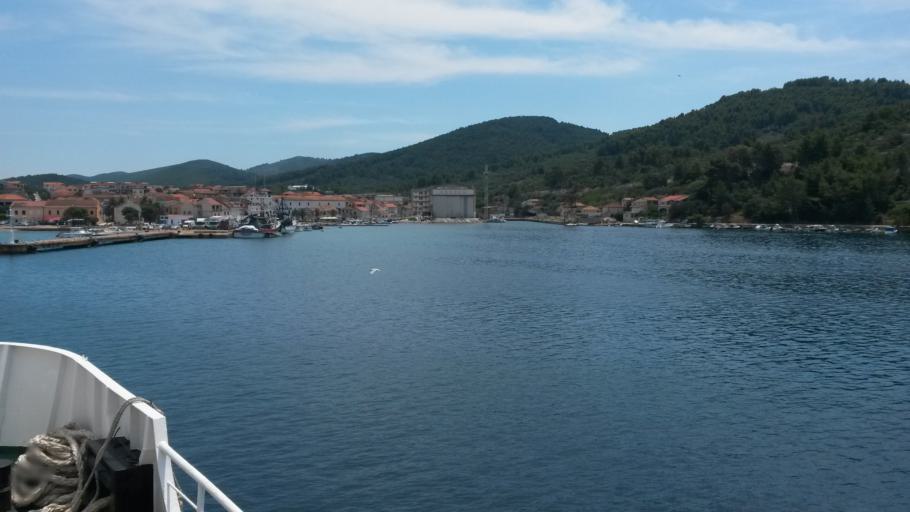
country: HR
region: Dubrovacko-Neretvanska
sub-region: Grad Dubrovnik
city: Vela Luka
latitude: 42.9605
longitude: 16.7085
